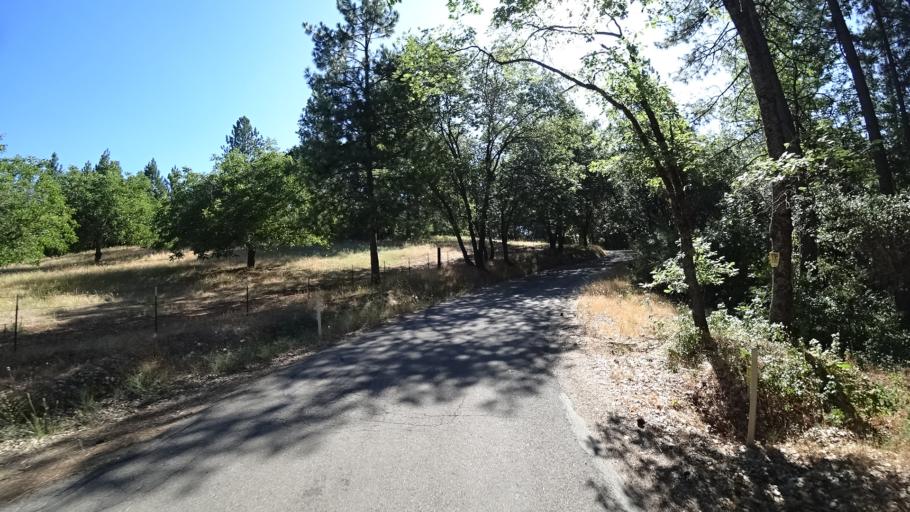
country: US
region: California
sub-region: Amador County
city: Pioneer
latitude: 38.4003
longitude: -120.5525
